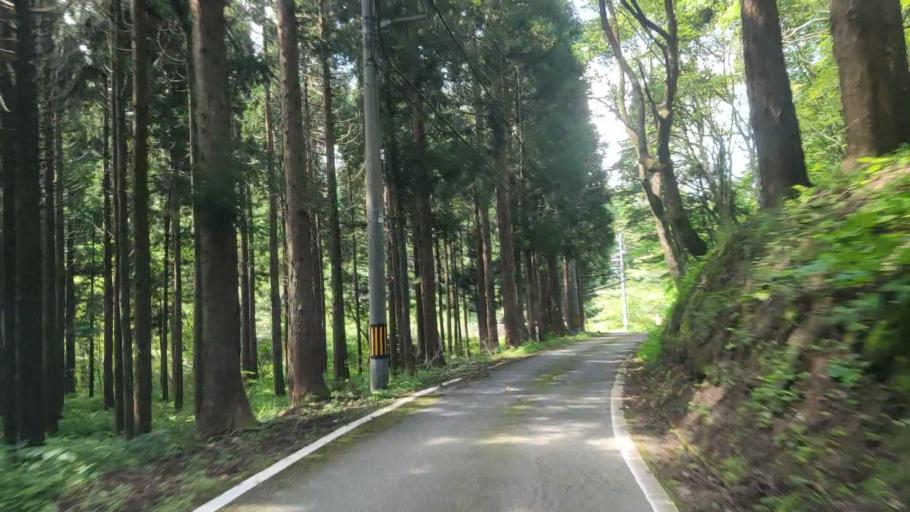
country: JP
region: Ishikawa
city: Komatsu
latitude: 36.2518
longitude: 136.5395
